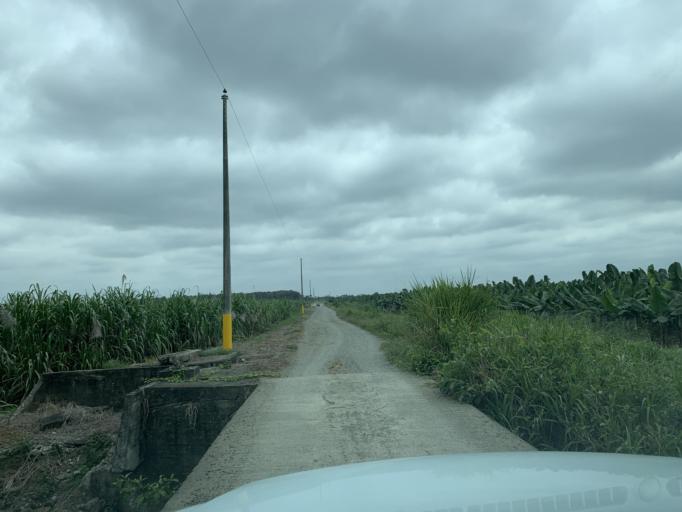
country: EC
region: Guayas
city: Coronel Marcelino Mariduena
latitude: -2.3362
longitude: -79.4559
